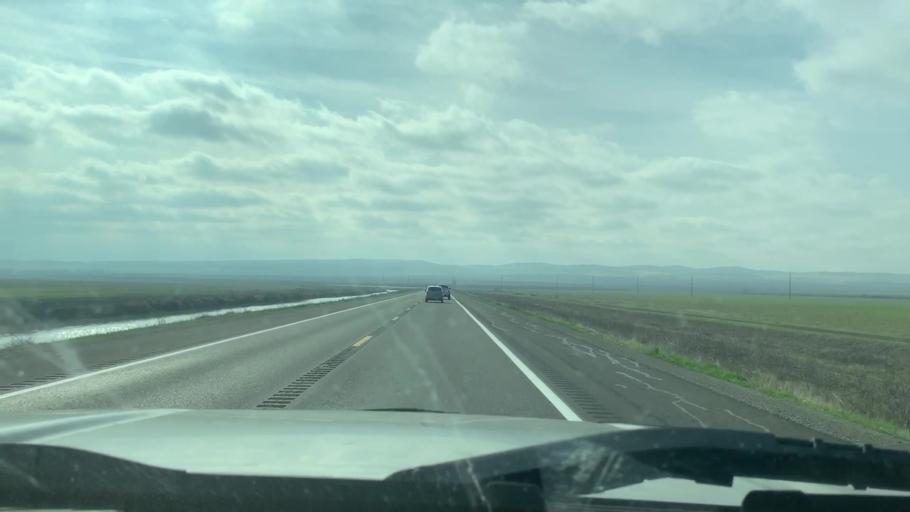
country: US
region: California
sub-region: Kings County
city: Kettleman City
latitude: 36.0441
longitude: -119.9514
